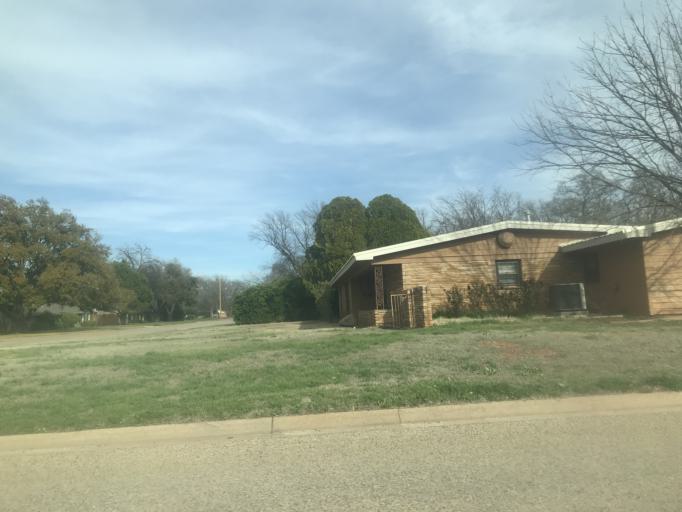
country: US
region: Texas
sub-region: Taylor County
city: Abilene
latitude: 32.4255
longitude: -99.7724
